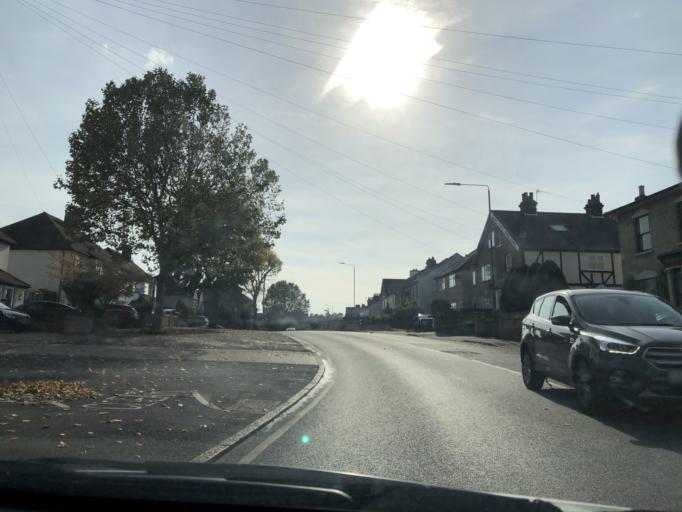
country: GB
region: England
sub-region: Greater London
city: Bexley
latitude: 51.4472
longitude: 0.1805
